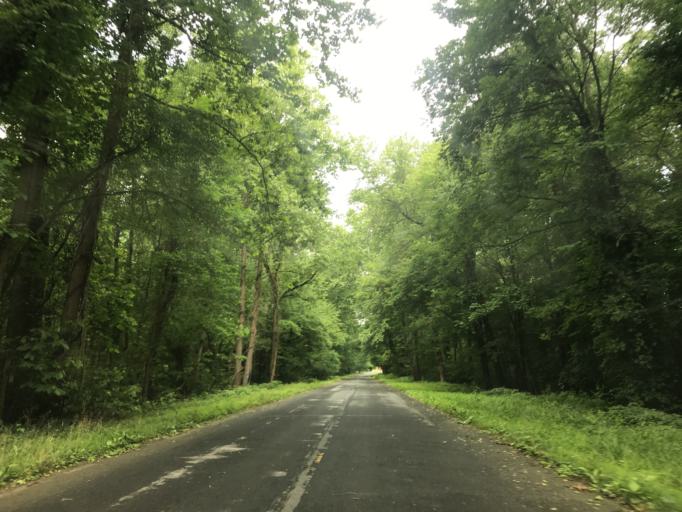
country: US
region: Maryland
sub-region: Caroline County
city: Ridgely
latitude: 38.9197
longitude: -75.9659
